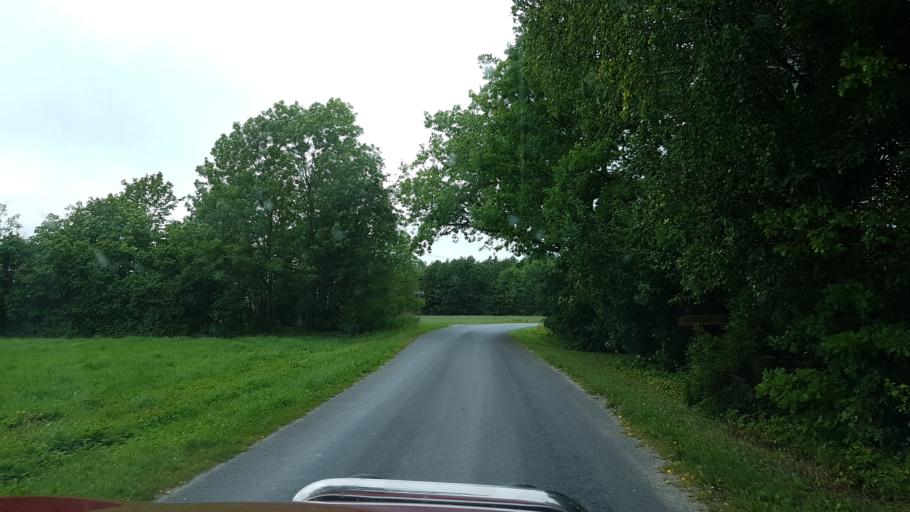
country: EE
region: Laeaene
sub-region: Ridala Parish
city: Uuemoisa
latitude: 59.0171
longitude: 23.7199
